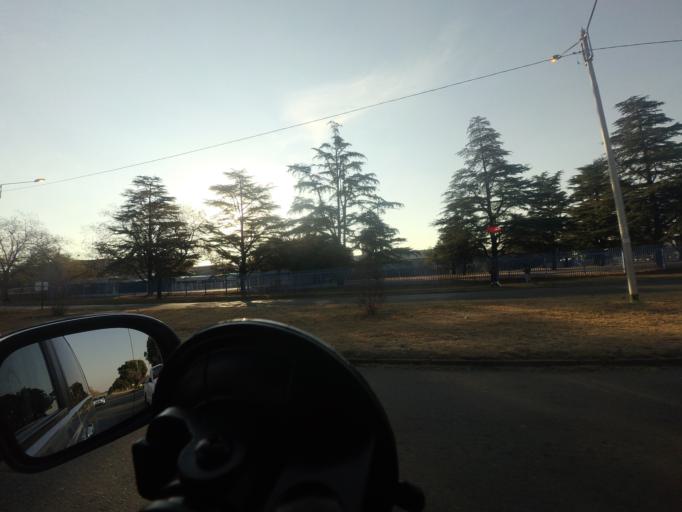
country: ZA
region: Gauteng
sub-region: Sedibeng District Municipality
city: Vereeniging
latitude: -26.6609
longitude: 27.9480
